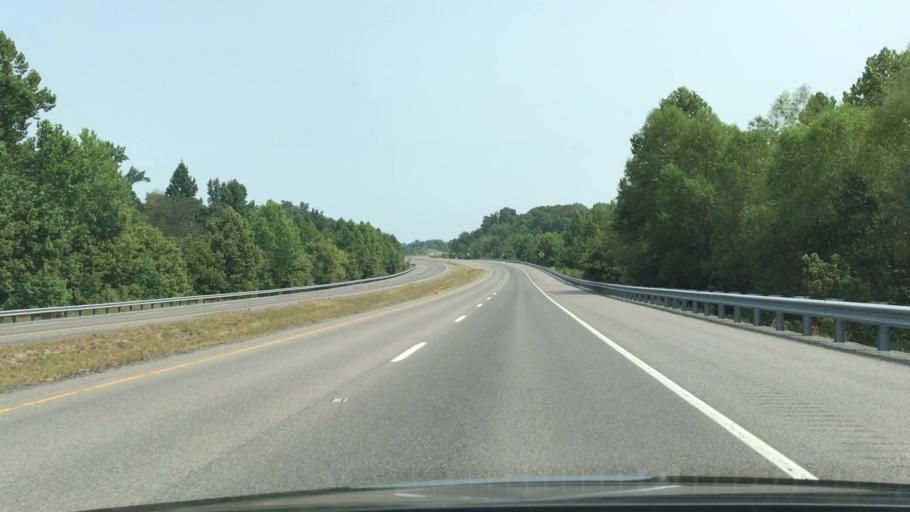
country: US
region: Kentucky
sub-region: Calloway County
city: Murray
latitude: 36.7558
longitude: -88.1526
